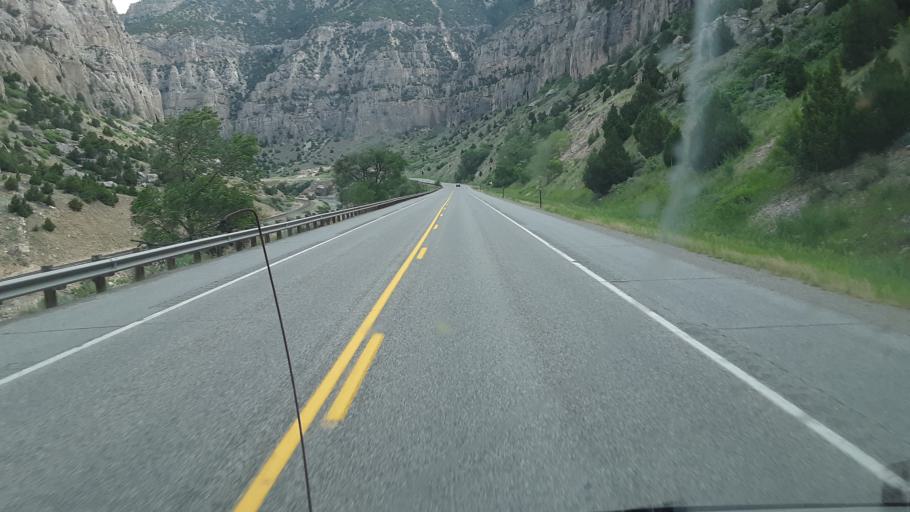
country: US
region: Wyoming
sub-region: Hot Springs County
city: Thermopolis
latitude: 43.5198
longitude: -108.1801
